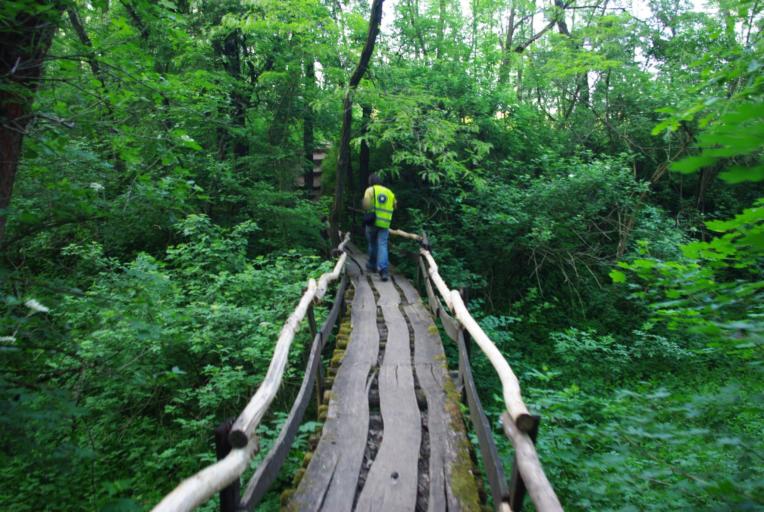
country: HU
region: Pest
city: Pilisszentivan
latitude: 47.6090
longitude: 18.8679
